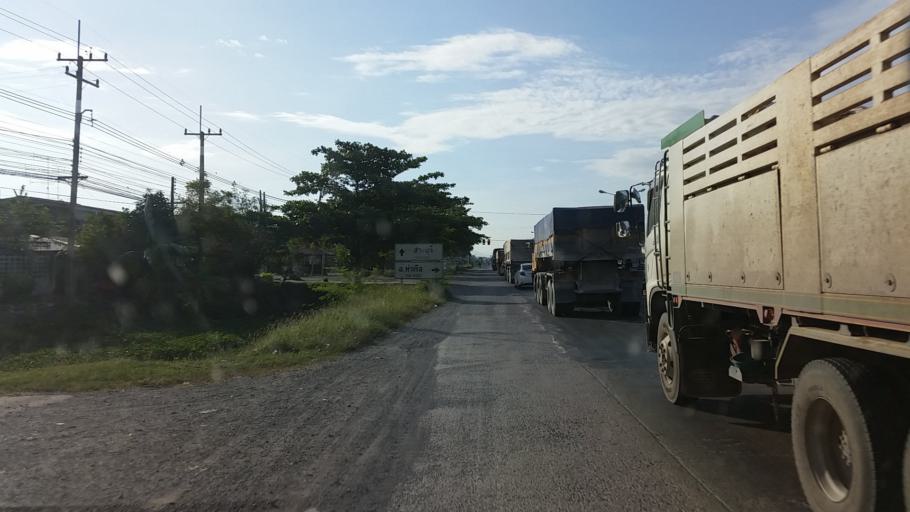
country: TH
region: Sara Buri
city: Chaloem Phra Kiat
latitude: 14.5873
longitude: 100.8991
